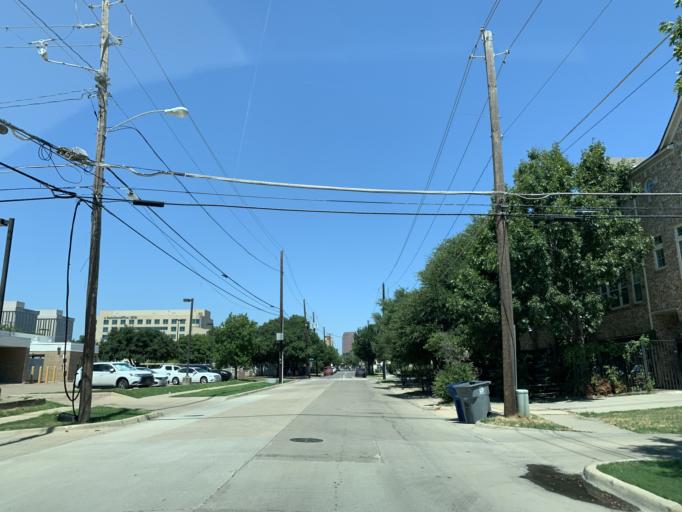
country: US
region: Texas
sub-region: Dallas County
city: Dallas
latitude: 32.7898
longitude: -96.7743
